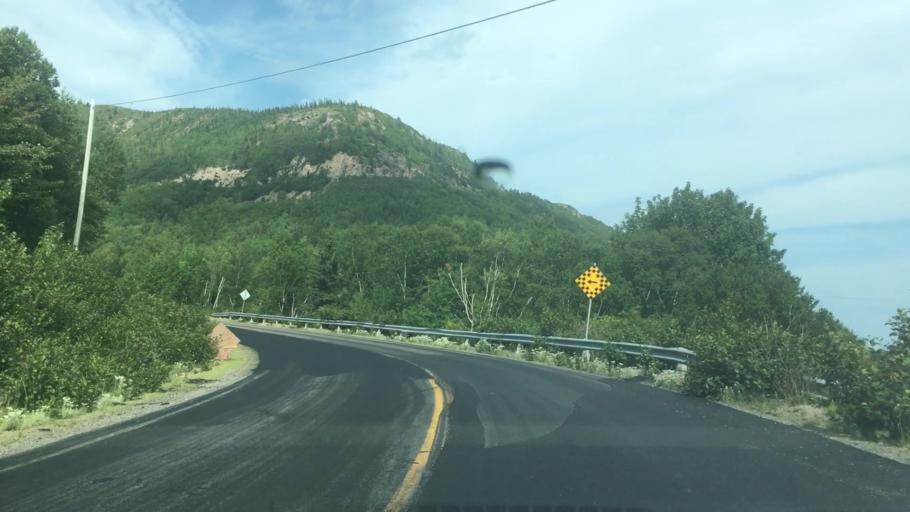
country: CA
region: Nova Scotia
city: Sydney Mines
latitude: 46.5774
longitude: -60.3892
